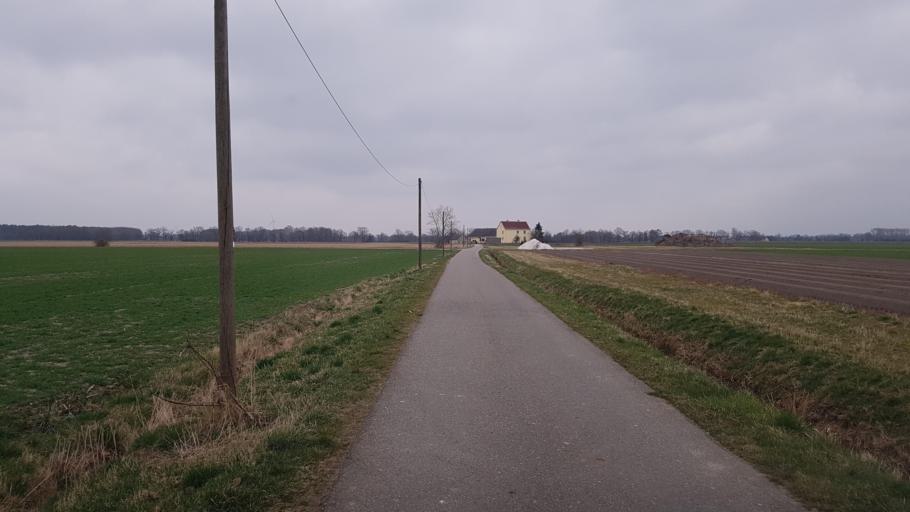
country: DE
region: Saxony
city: Nauwalde
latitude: 51.4219
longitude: 13.4115
